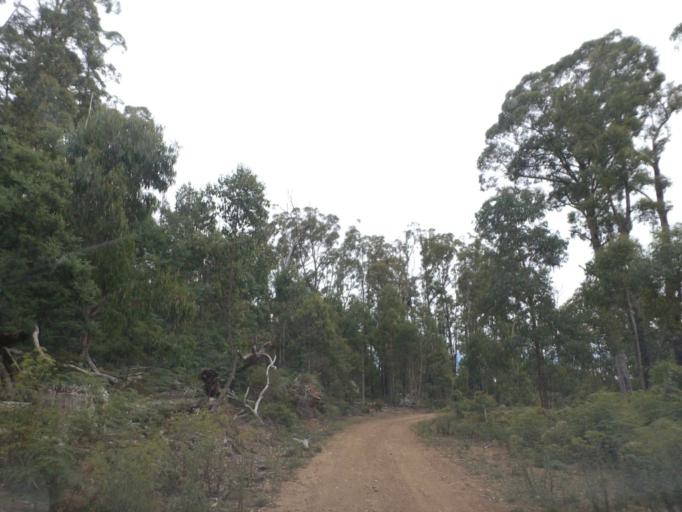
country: AU
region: Victoria
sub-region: Murrindindi
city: Alexandra
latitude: -37.3898
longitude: 145.5738
